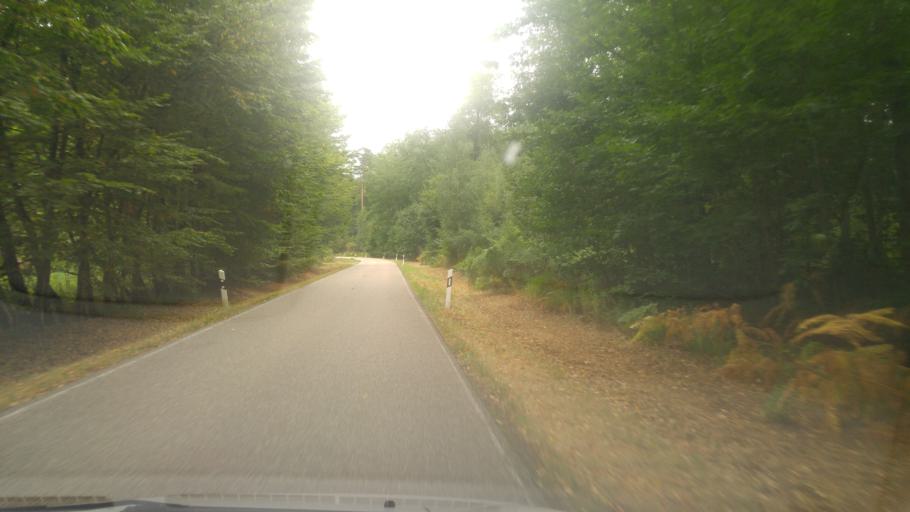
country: DE
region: Rheinland-Pfalz
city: Scheibenhardt
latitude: 48.9927
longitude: 8.0936
